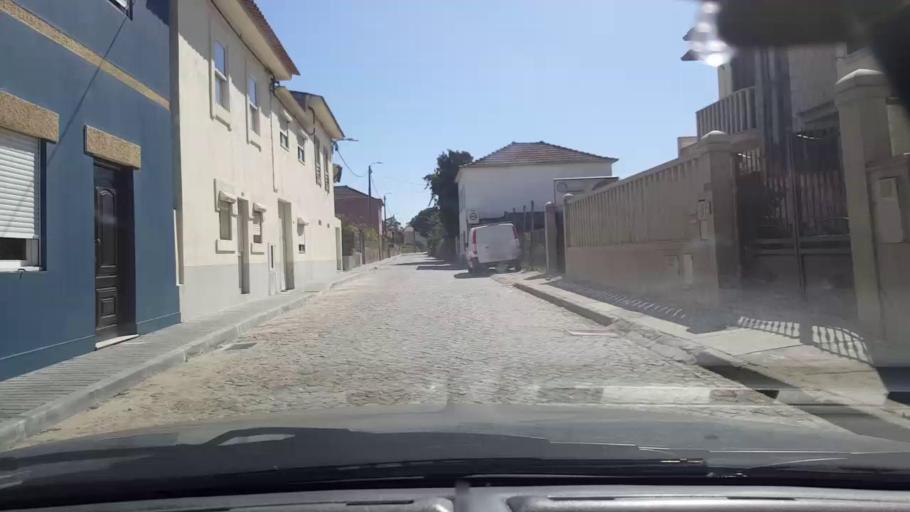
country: PT
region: Porto
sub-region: Vila do Conde
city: Arvore
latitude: 41.3110
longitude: -8.7188
